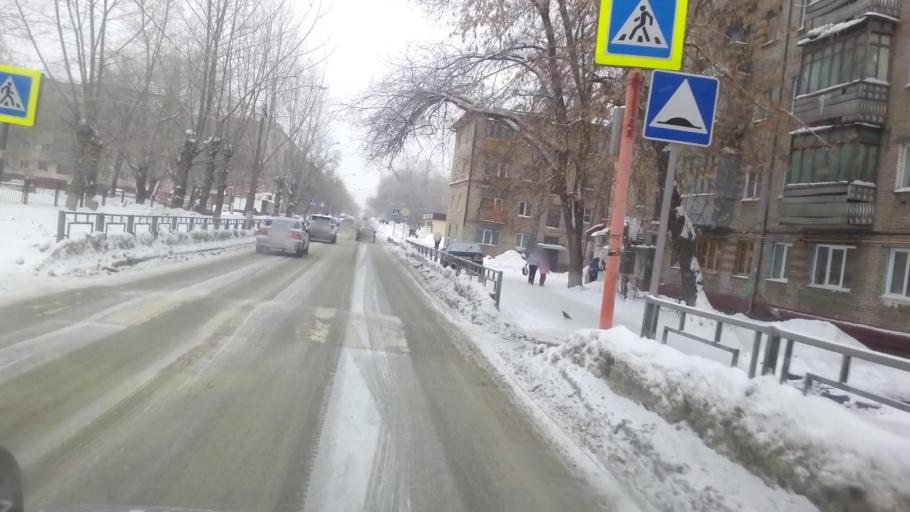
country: RU
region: Altai Krai
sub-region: Gorod Barnaulskiy
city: Barnaul
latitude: 53.3793
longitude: 83.7170
